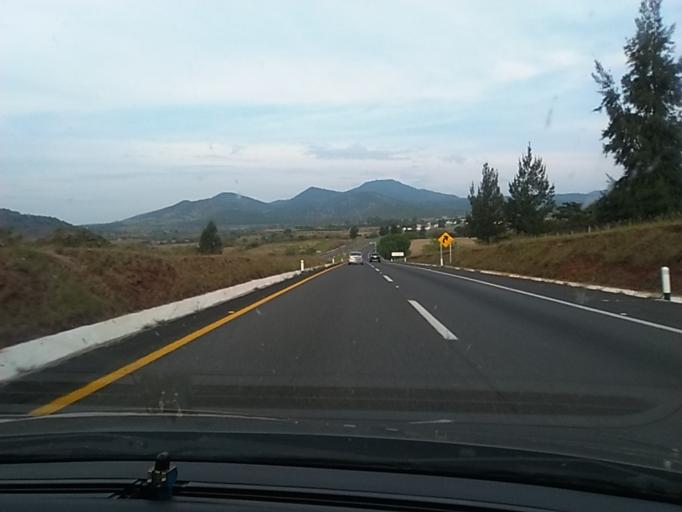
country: MX
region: Michoacan
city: Zinapecuaro
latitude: 19.9026
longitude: -100.8037
